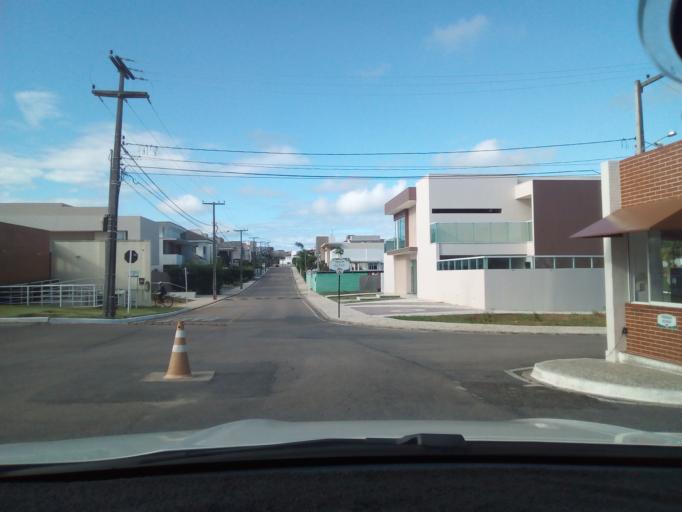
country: BR
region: Paraiba
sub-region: Joao Pessoa
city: Joao Pessoa
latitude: -7.1550
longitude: -34.8181
